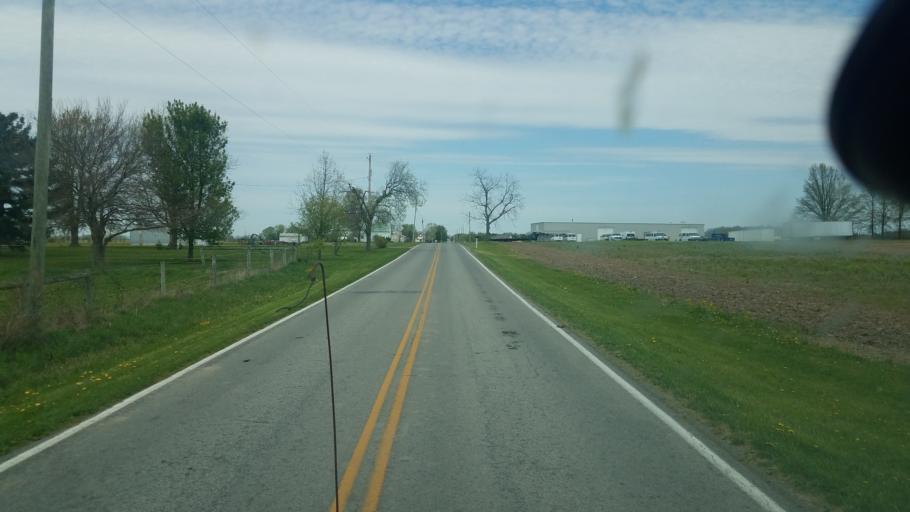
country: US
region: Ohio
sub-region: Allen County
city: Bluffton
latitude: 40.8031
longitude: -83.9758
